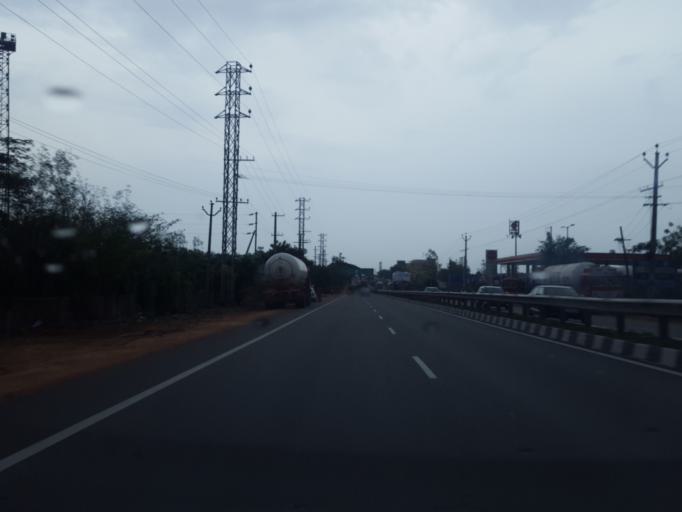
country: IN
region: Telangana
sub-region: Rangareddi
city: Sriramnagar
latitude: 17.1566
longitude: 78.2936
